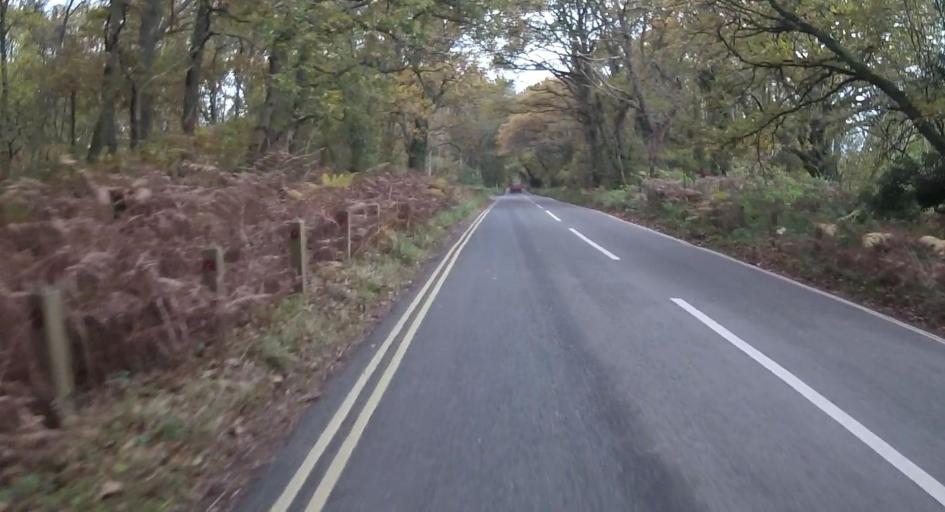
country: GB
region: England
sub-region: Surrey
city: Churt
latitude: 51.1596
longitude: -0.7949
